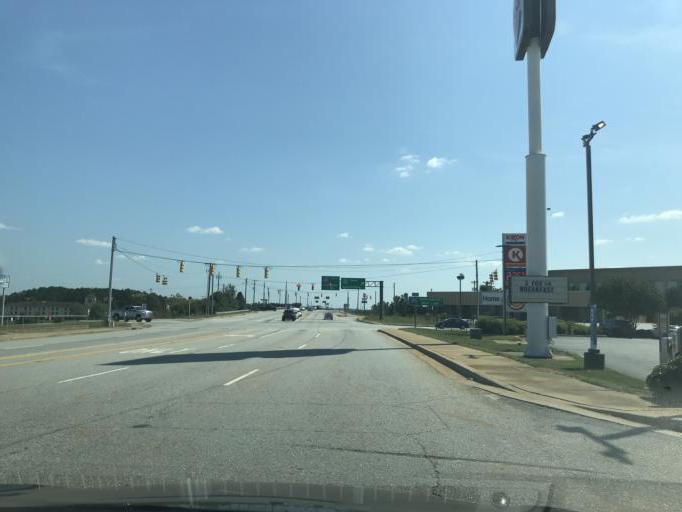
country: US
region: South Carolina
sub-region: Cherokee County
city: Gaffney
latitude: 35.0849
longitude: -81.7080
